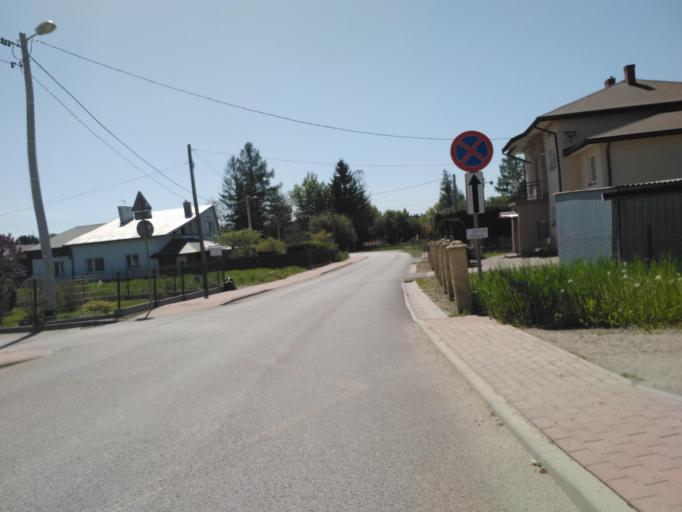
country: PL
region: Subcarpathian Voivodeship
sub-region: Powiat krosnienski
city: Miejsce Piastowe
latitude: 49.6487
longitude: 21.8027
